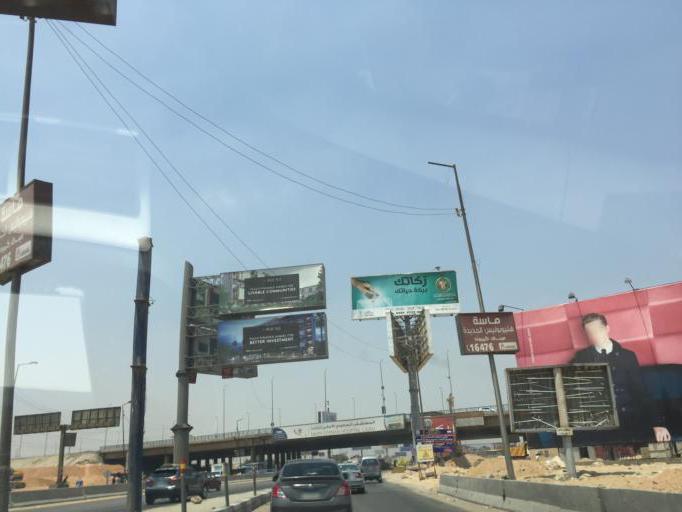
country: EG
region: Muhafazat al Qalyubiyah
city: Al Khankah
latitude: 30.0799
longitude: 31.4370
